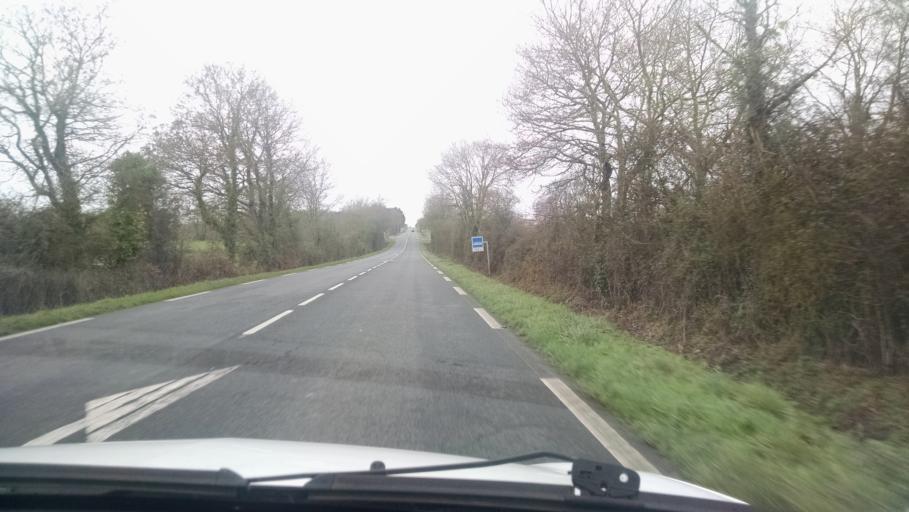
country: FR
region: Pays de la Loire
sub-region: Departement de la Loire-Atlantique
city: Boussay
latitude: 47.0646
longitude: -1.1988
